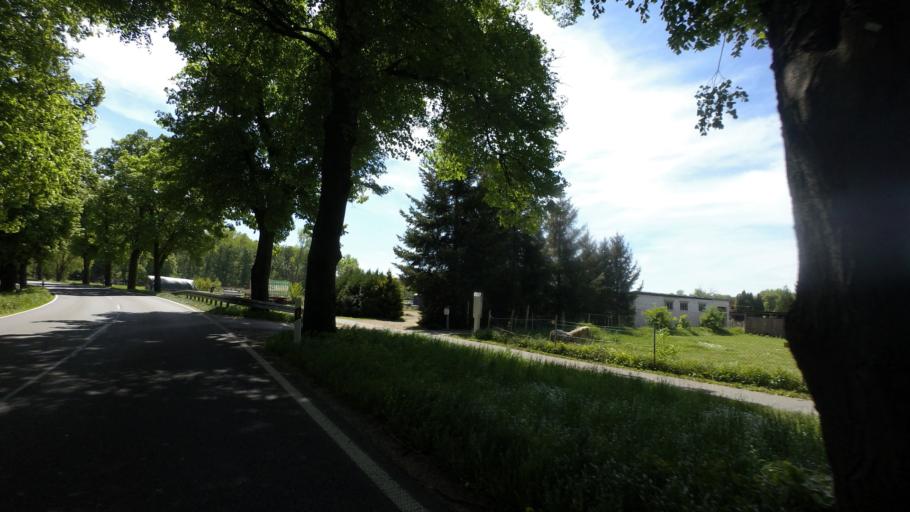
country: DE
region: Brandenburg
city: Luckenwalde
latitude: 52.0766
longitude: 13.1844
